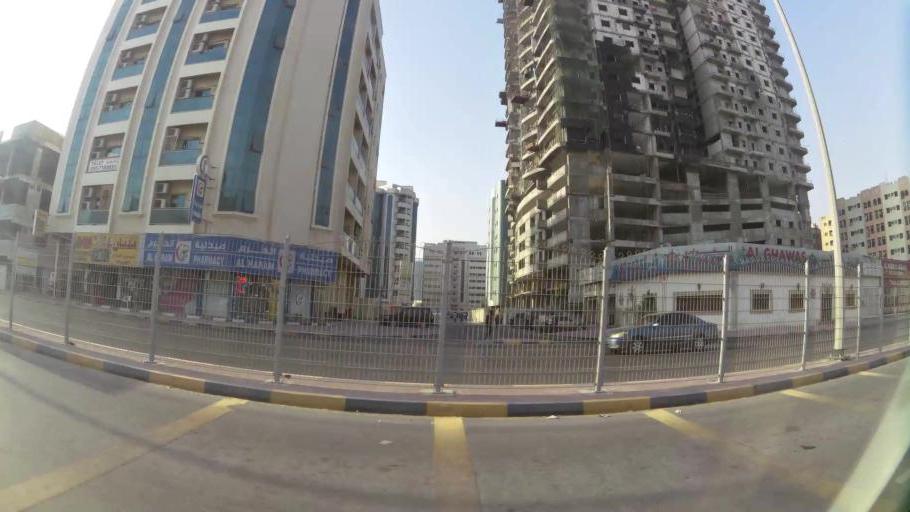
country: AE
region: Ajman
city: Ajman
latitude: 25.3866
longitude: 55.4535
